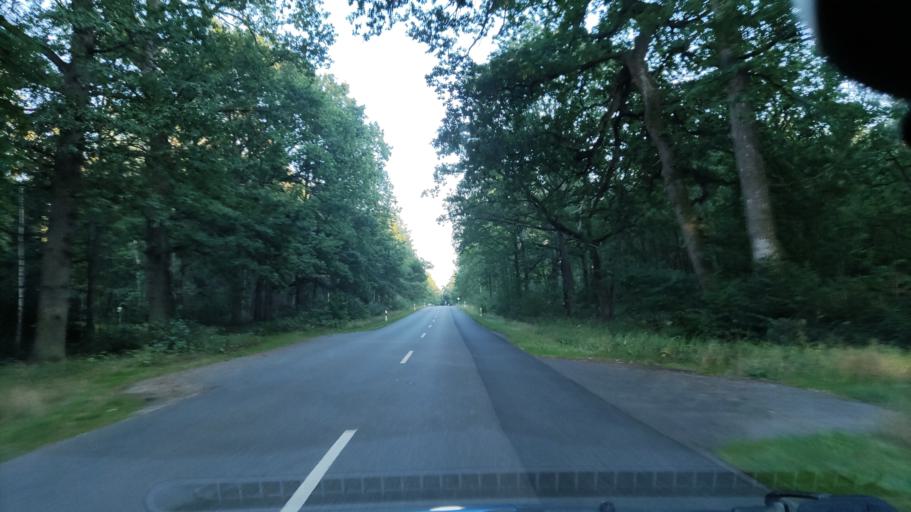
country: DE
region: Lower Saxony
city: Fassberg
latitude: 52.9674
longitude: 10.1657
